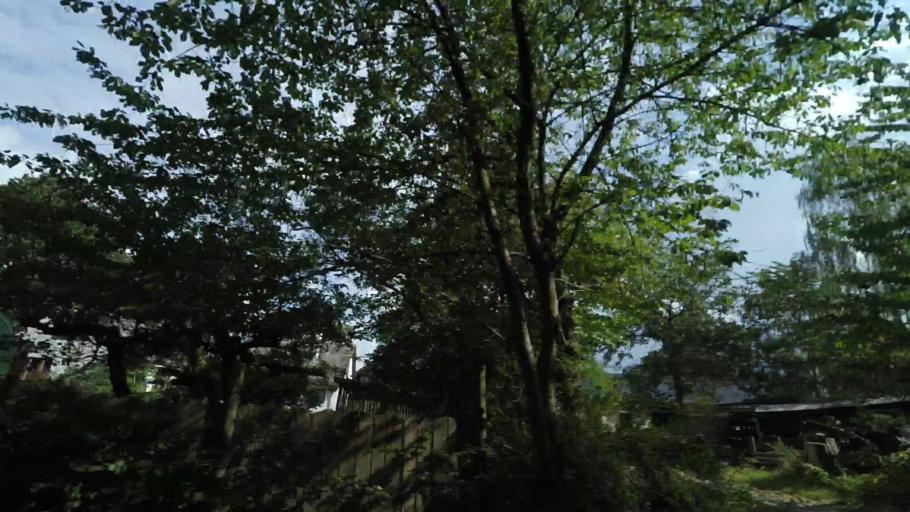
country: DK
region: Central Jutland
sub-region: Syddjurs Kommune
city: Ryomgard
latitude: 56.4622
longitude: 10.5271
